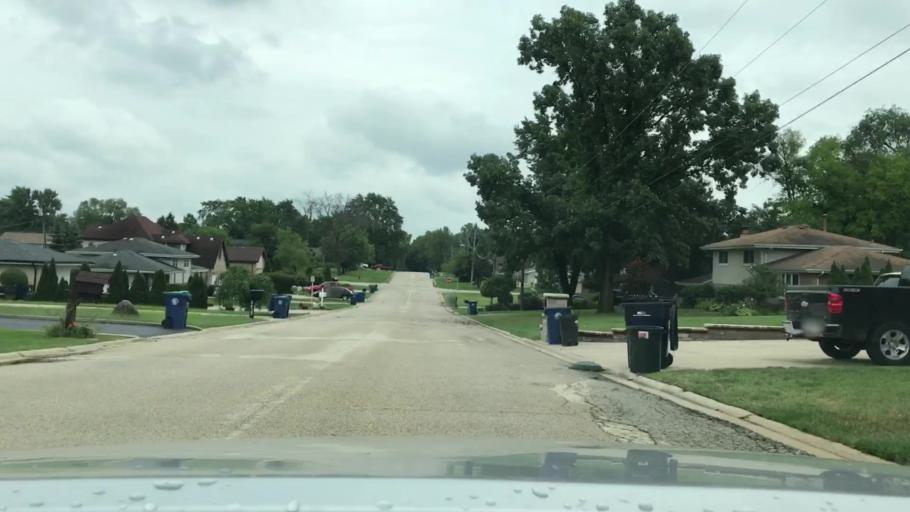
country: US
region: Illinois
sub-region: Cook County
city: Justice
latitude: 41.7380
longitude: -87.8285
